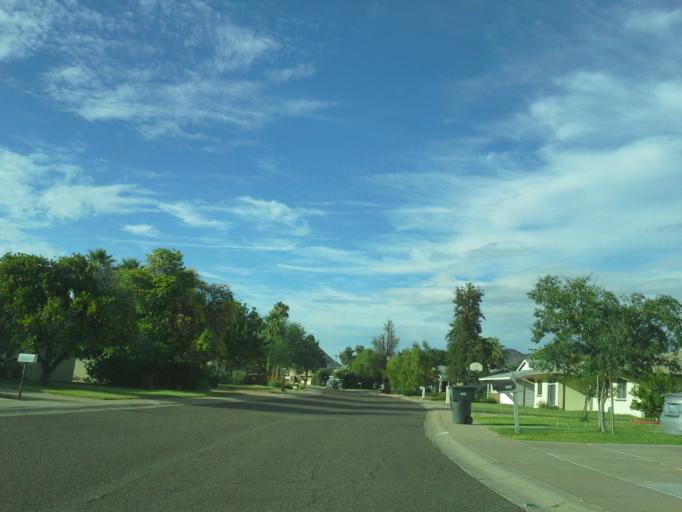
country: US
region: Arizona
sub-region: Maricopa County
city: Glendale
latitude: 33.5648
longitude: -112.0961
